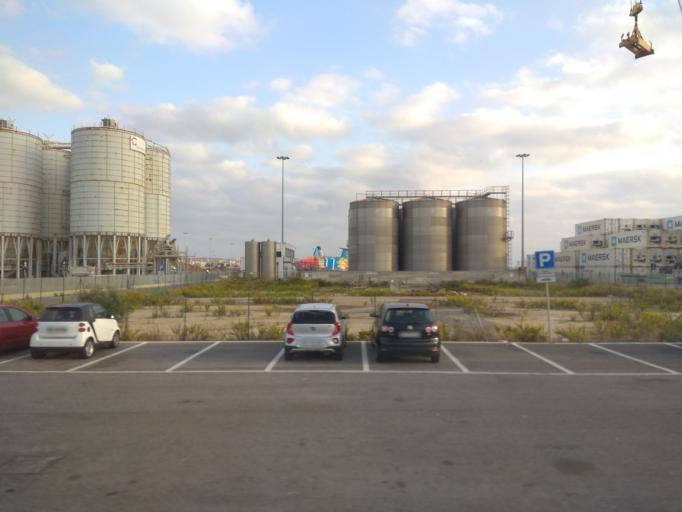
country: IT
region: Latium
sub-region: Citta metropolitana di Roma Capitale
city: Civitavecchia
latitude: 42.1039
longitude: 11.7765
